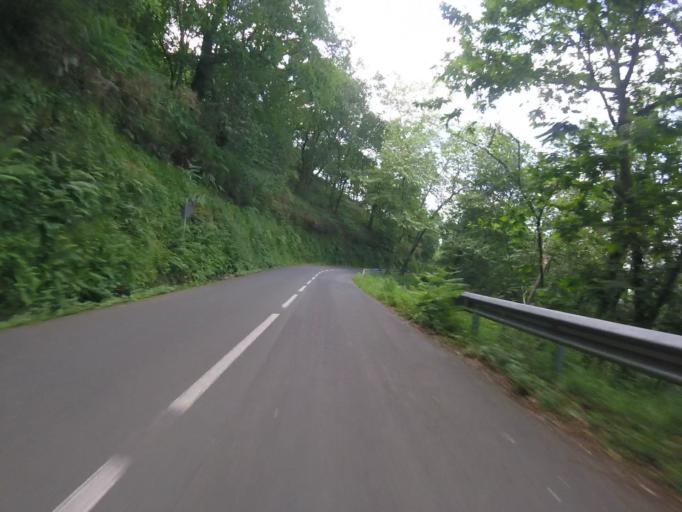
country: ES
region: Basque Country
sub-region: Provincia de Guipuzcoa
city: Errenteria
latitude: 43.2750
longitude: -1.8490
